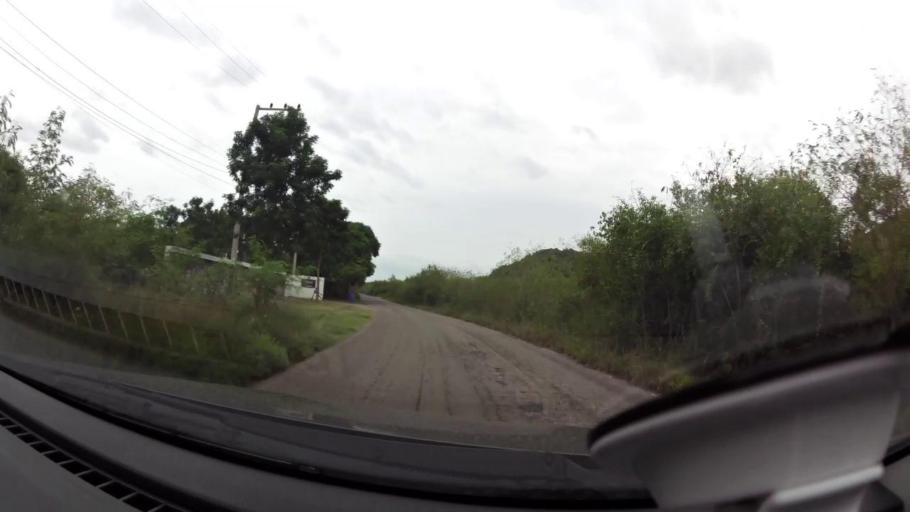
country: TH
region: Prachuap Khiri Khan
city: Pran Buri
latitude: 12.4235
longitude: 99.9793
